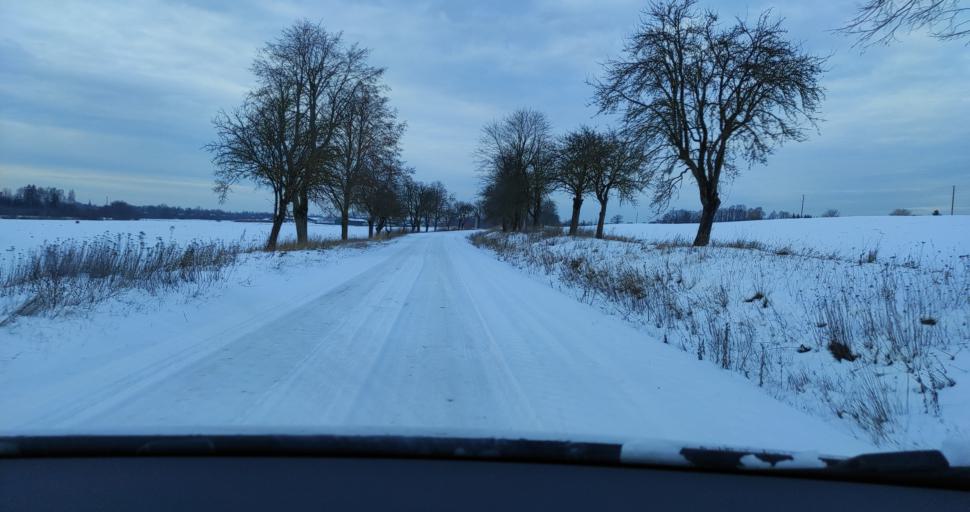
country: LV
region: Kuldigas Rajons
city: Kuldiga
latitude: 56.9498
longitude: 22.0197
